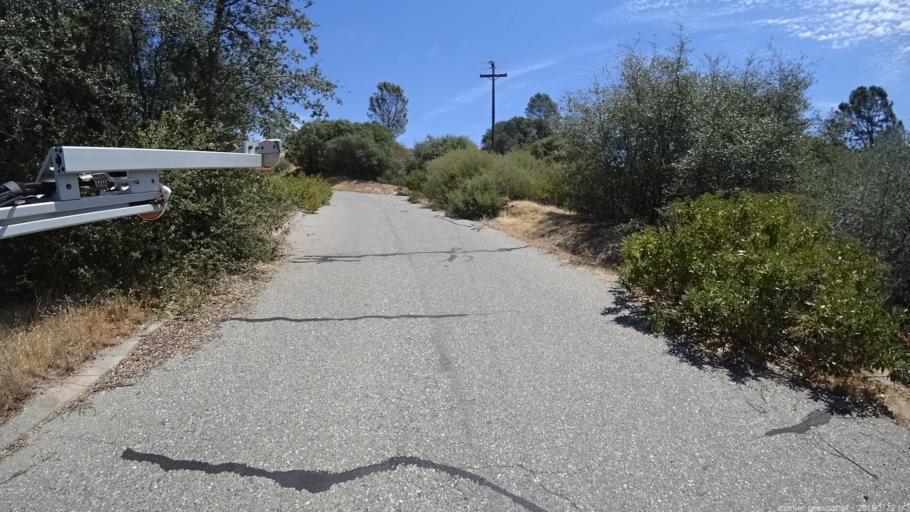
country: US
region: California
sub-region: Madera County
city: Coarsegold
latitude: 37.2412
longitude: -119.7292
